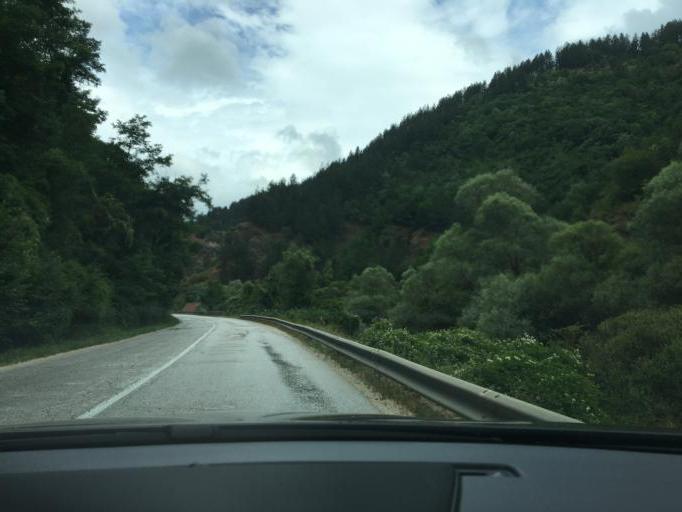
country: MK
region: Kriva Palanka
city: Kriva Palanka
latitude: 42.2284
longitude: 22.3811
